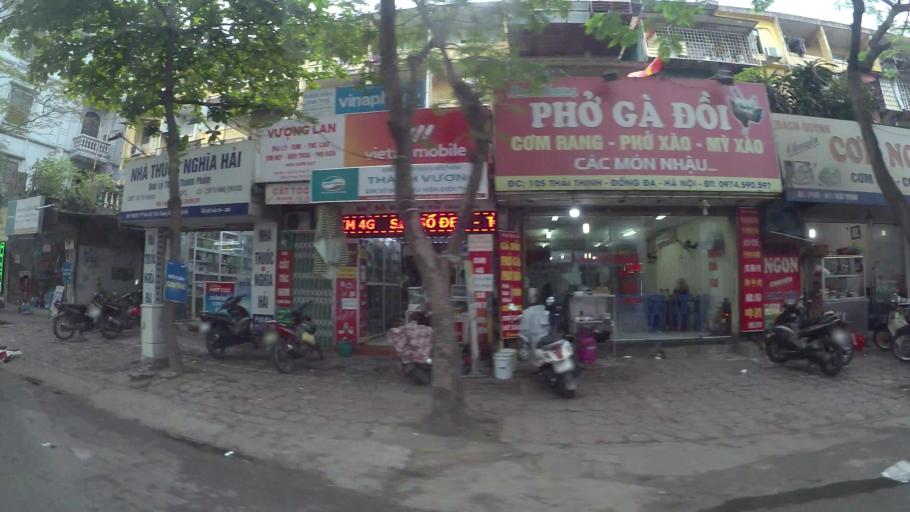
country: VN
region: Ha Noi
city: Dong Da
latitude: 21.0095
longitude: 105.8193
